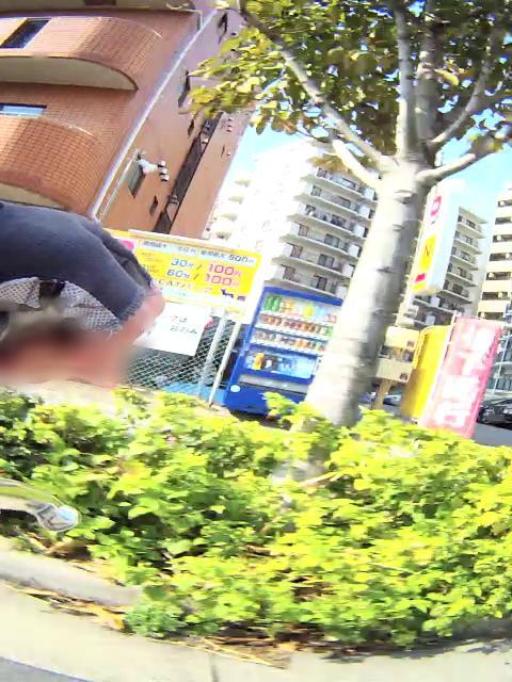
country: JP
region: Osaka
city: Suita
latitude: 34.7380
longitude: 135.5028
